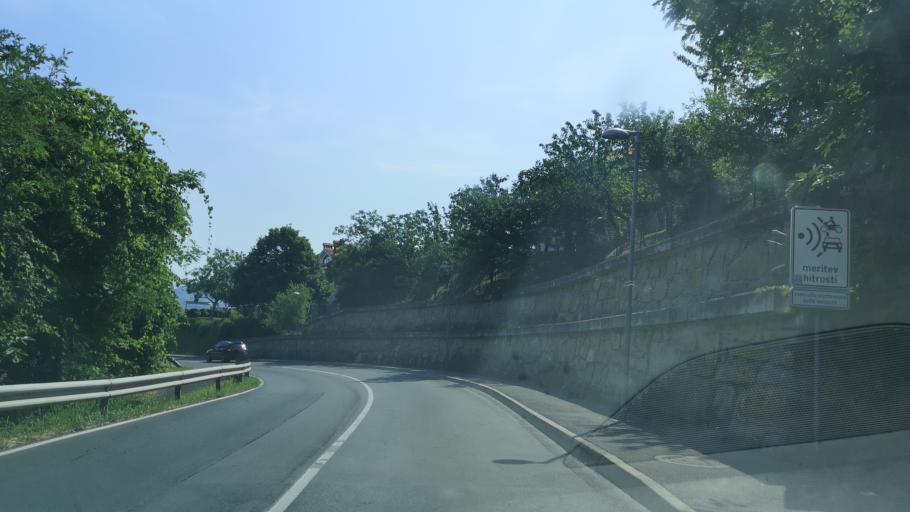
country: SI
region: Izola-Isola
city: Jagodje
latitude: 45.5304
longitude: 13.6417
